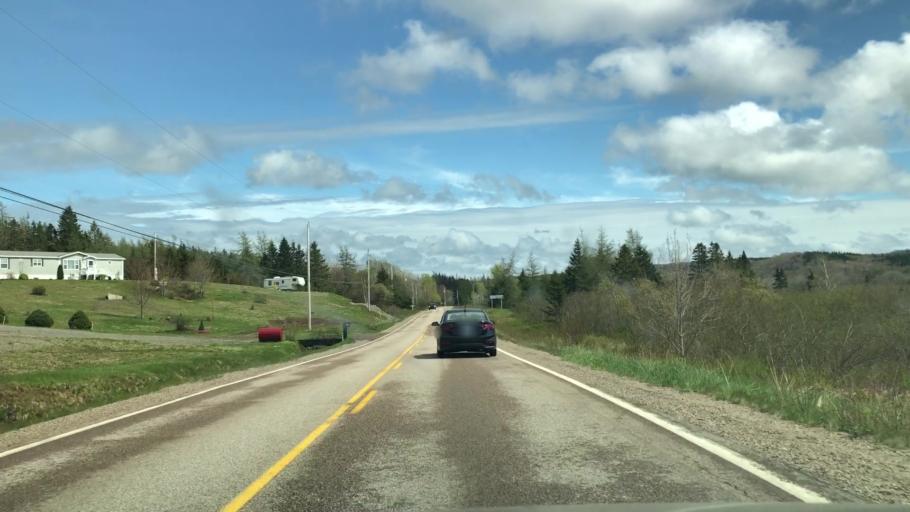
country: CA
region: Nova Scotia
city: Antigonish
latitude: 45.1879
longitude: -61.9872
